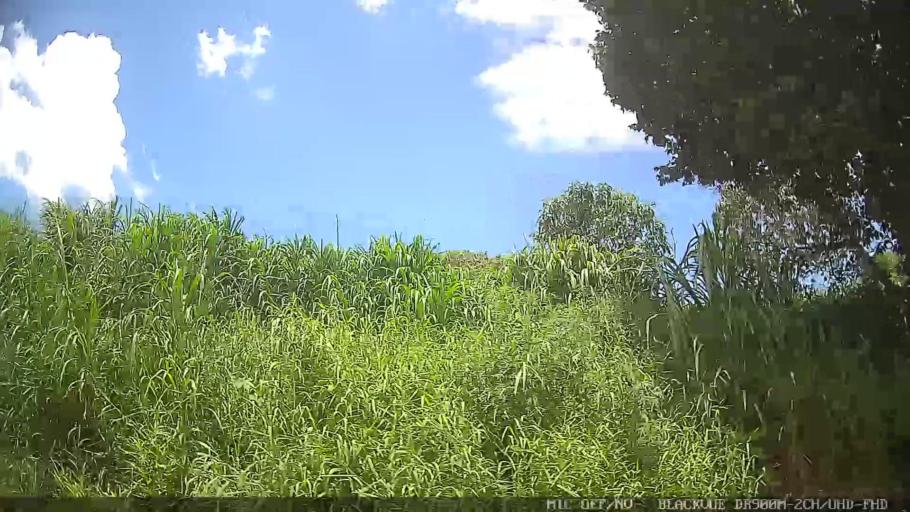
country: BR
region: Sao Paulo
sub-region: Biritiba-Mirim
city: Biritiba Mirim
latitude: -23.6025
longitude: -46.0531
